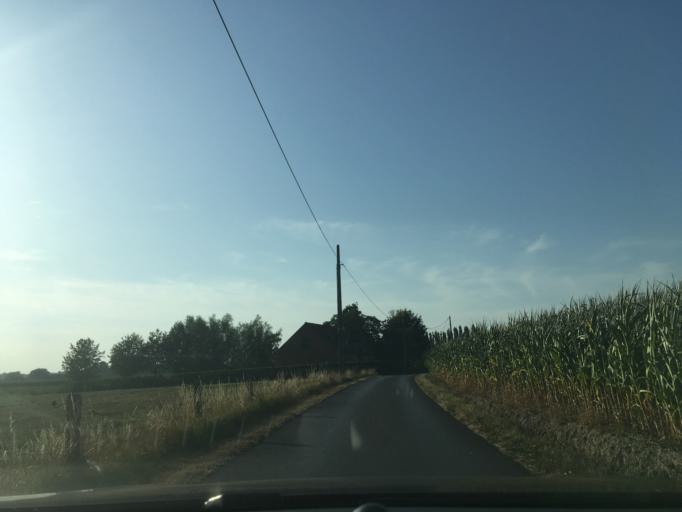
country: BE
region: Flanders
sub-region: Provincie West-Vlaanderen
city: Tielt
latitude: 50.9912
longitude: 3.3700
